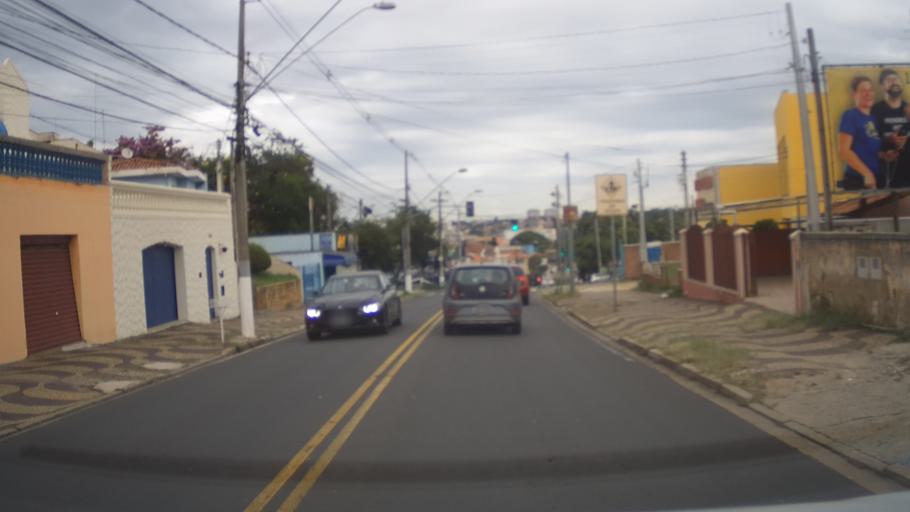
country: BR
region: Sao Paulo
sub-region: Campinas
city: Campinas
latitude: -22.9200
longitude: -47.0567
